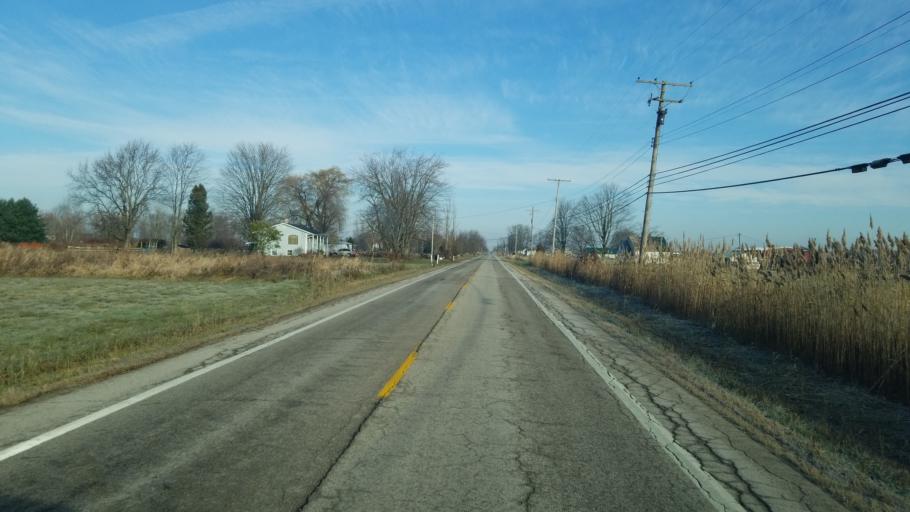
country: US
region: Ohio
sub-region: Ashtabula County
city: Jefferson
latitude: 41.7375
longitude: -80.6673
